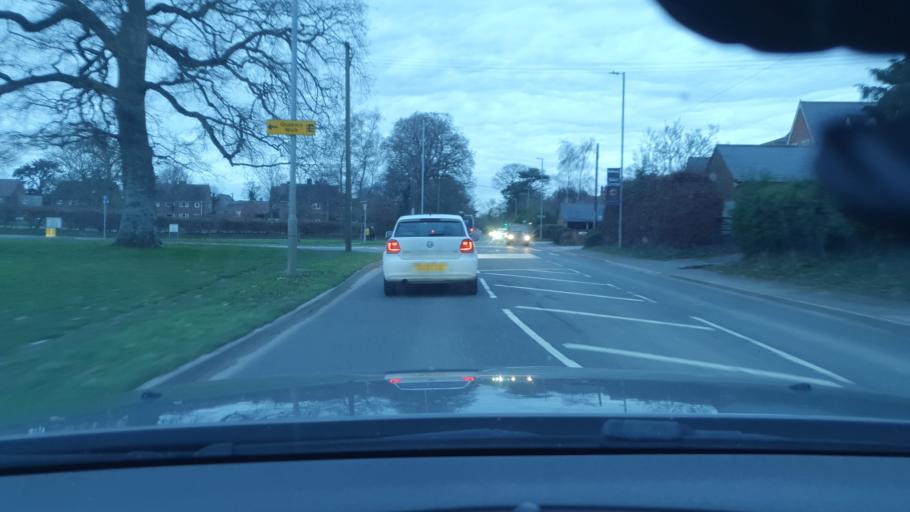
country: GB
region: England
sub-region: Wiltshire
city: Devizes
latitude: 51.3573
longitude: -1.9817
